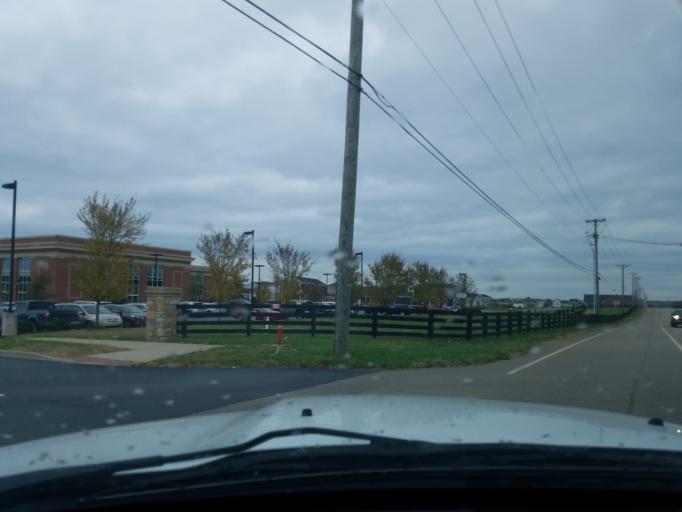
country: US
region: Kentucky
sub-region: Jefferson County
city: Worthington
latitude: 38.3286
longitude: -85.5613
